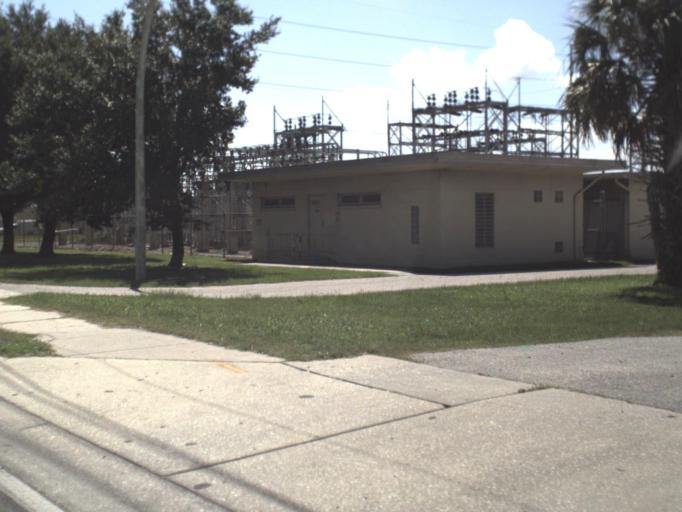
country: US
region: Florida
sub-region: Pinellas County
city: Largo
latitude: 27.9166
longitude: -82.7739
